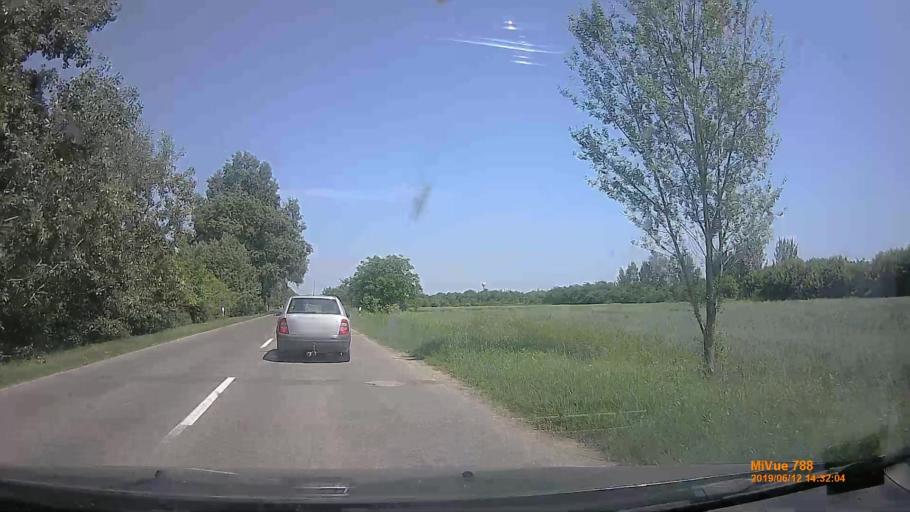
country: HU
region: Csongrad
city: Kiszombor
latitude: 46.1929
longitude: 20.4156
